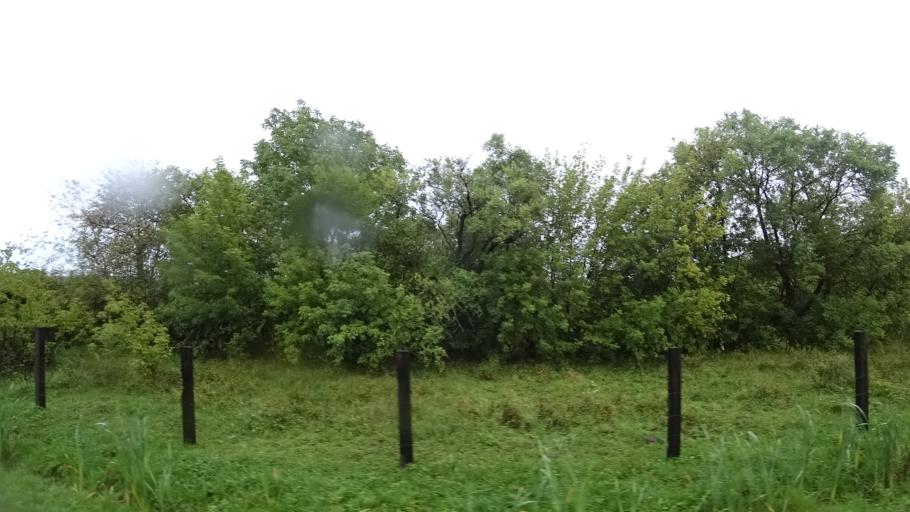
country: RU
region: Primorskiy
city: Monastyrishche
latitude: 44.2513
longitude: 132.4259
